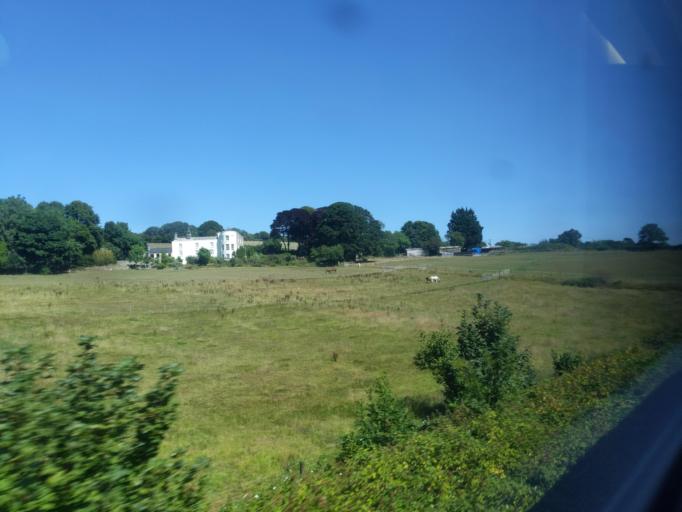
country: GB
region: England
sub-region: Devon
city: Ivybridge
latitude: 50.3962
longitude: -3.9163
